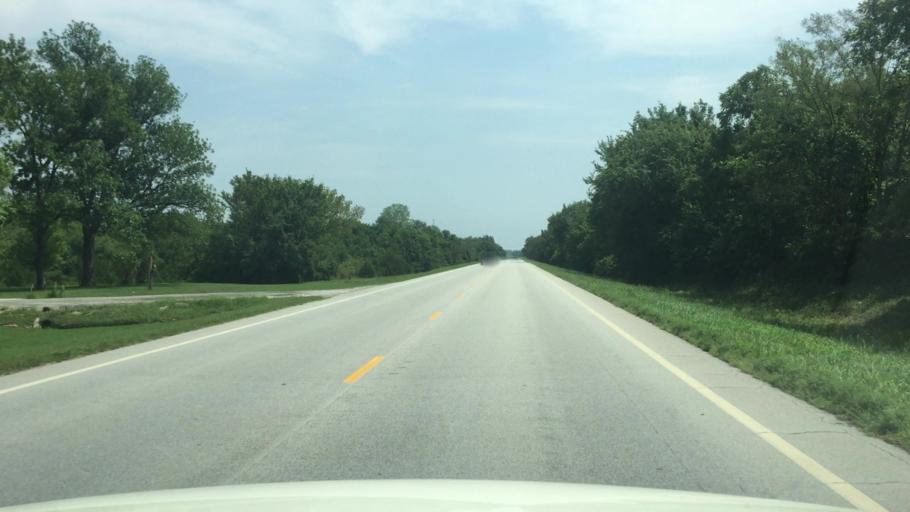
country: US
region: Kansas
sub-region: Cherokee County
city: Columbus
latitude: 37.1788
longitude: -94.8779
